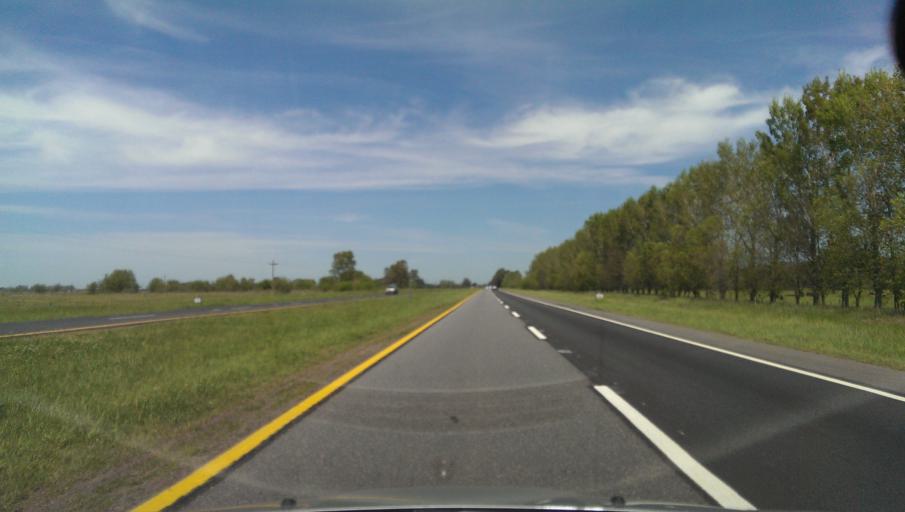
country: AR
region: Buenos Aires
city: San Miguel del Monte
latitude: -35.3499
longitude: -58.7965
